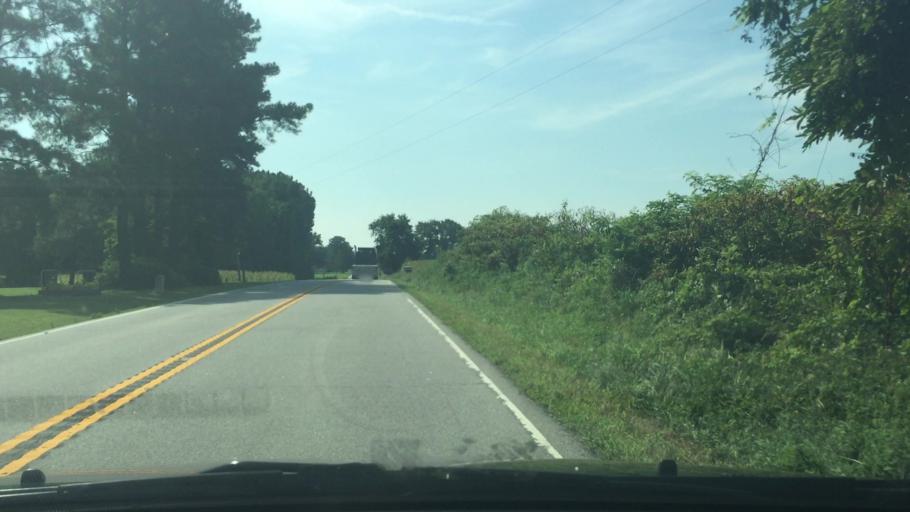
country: US
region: Virginia
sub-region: Sussex County
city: Sussex
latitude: 36.8819
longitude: -77.1527
